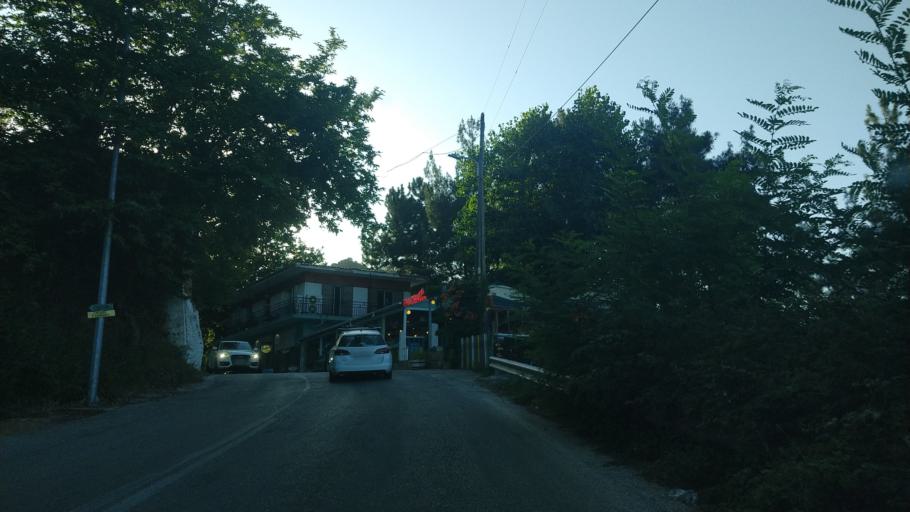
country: GR
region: East Macedonia and Thrace
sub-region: Nomos Kavalas
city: Potamia
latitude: 40.7294
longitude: 24.7318
